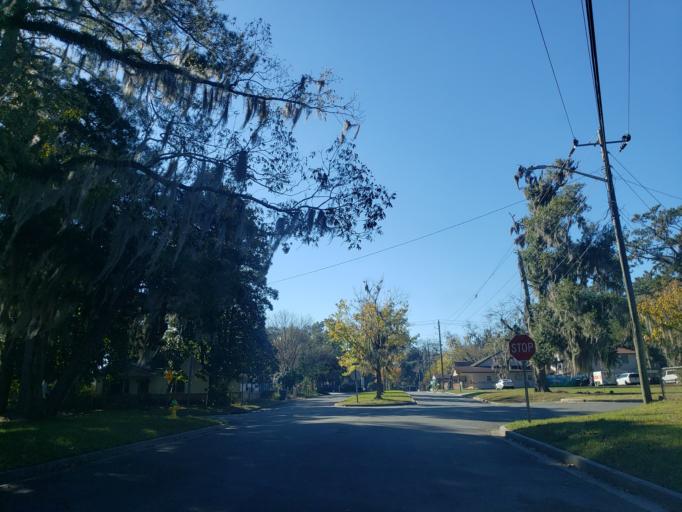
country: US
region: Georgia
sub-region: Chatham County
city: Isle of Hope
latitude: 31.9960
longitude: -81.1026
